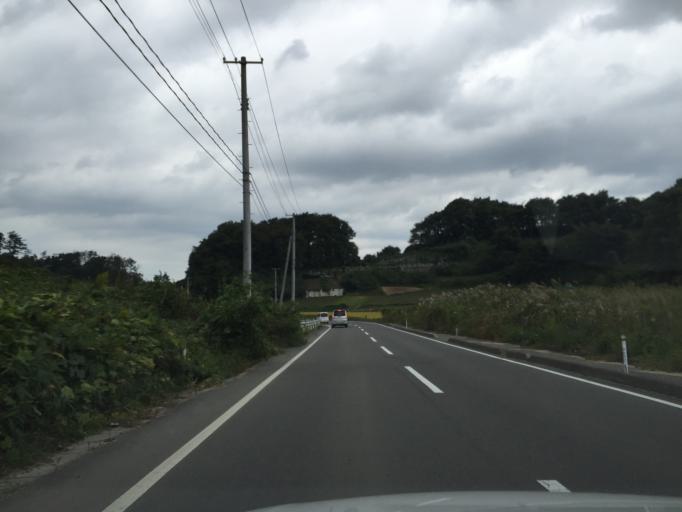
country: JP
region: Fukushima
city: Miharu
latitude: 37.4308
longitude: 140.5153
